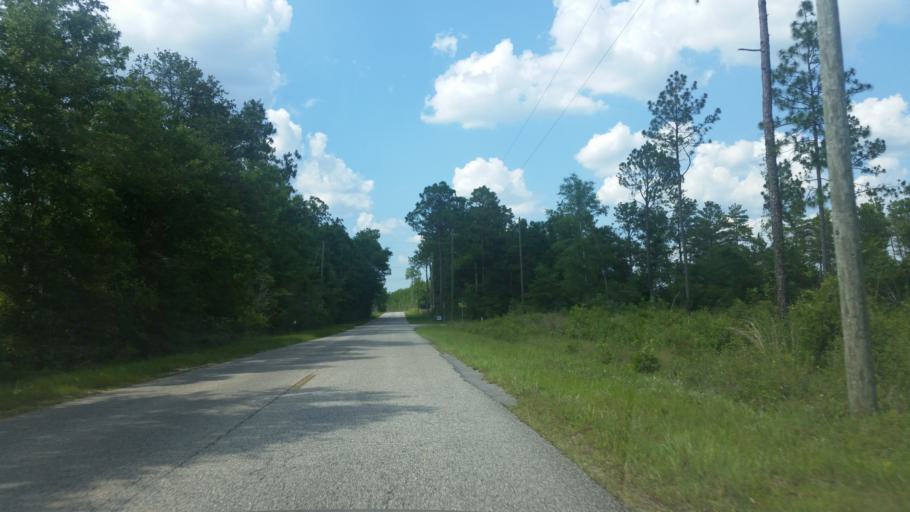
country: US
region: Florida
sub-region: Santa Rosa County
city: East Milton
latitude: 30.6701
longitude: -86.8774
